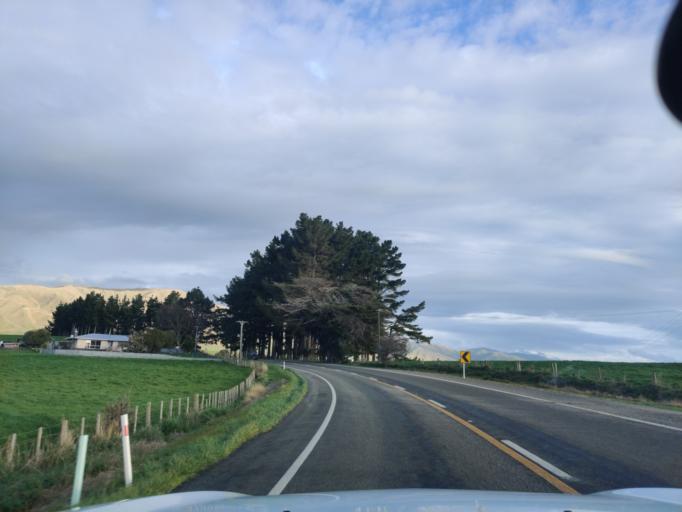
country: NZ
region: Manawatu-Wanganui
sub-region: Palmerston North City
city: Palmerston North
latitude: -40.4922
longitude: 175.4922
